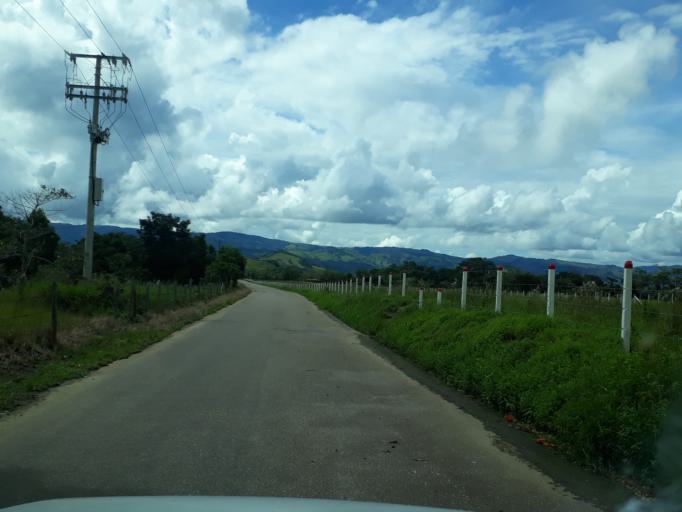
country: CO
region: Cundinamarca
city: Medina
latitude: 4.6436
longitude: -73.3206
